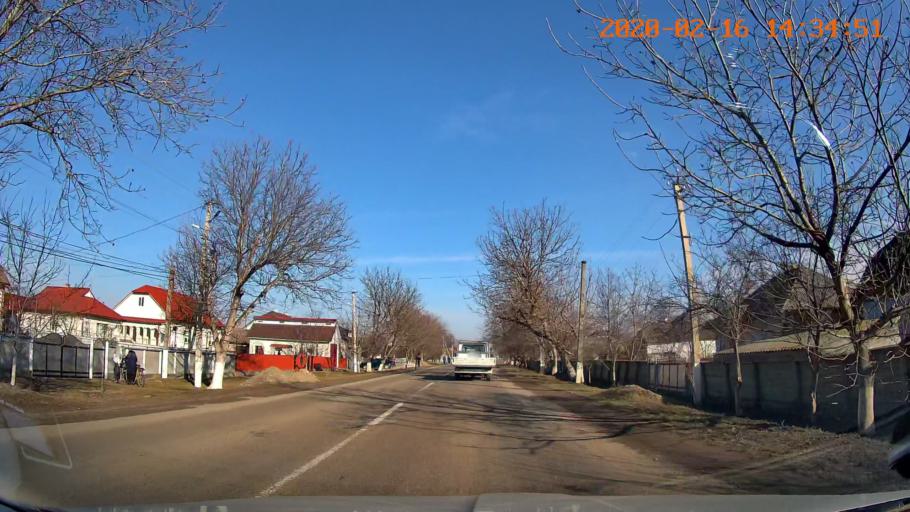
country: RO
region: Botosani
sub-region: Comuna Darabani
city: Bajura
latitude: 48.2219
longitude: 26.4843
